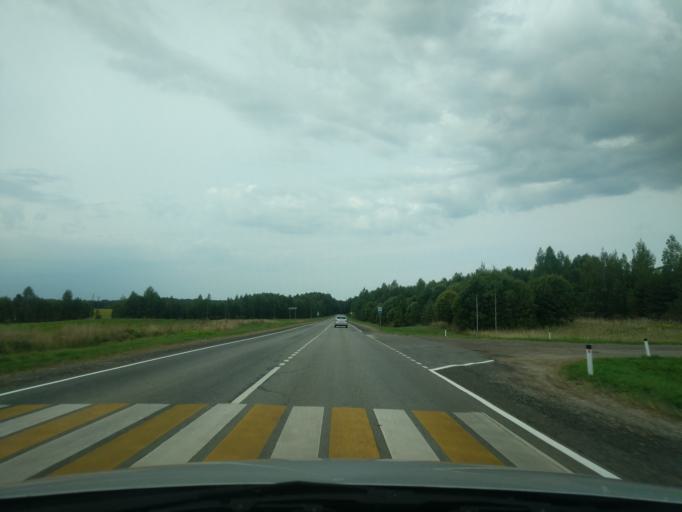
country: RU
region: Kirov
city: Svecha
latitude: 58.2724
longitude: 47.7380
